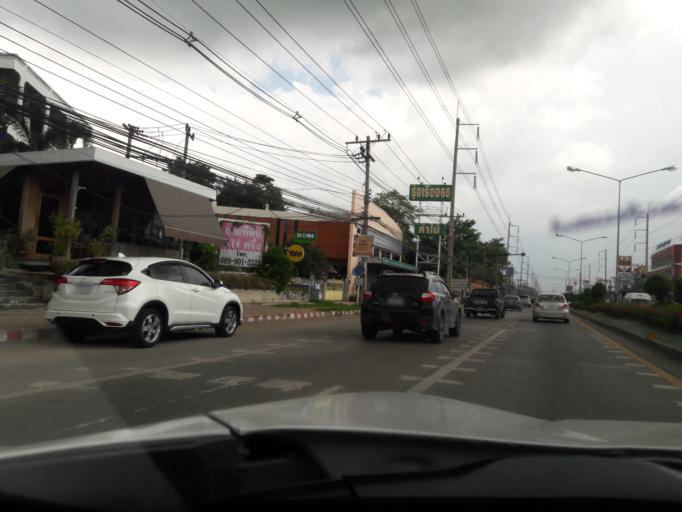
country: TH
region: Lop Buri
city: Lop Buri
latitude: 14.7869
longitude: 100.6791
